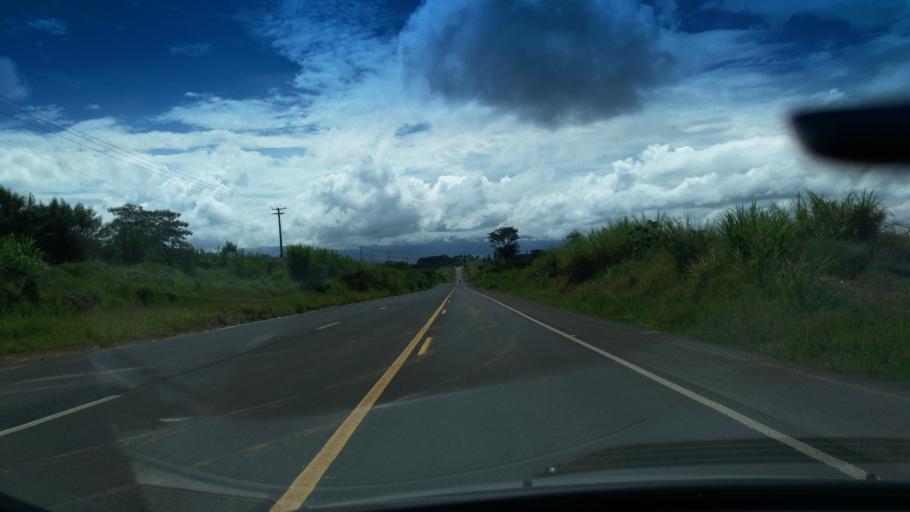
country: BR
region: Sao Paulo
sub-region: Santo Antonio Do Jardim
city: Espirito Santo do Pinhal
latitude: -22.1503
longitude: -46.7203
